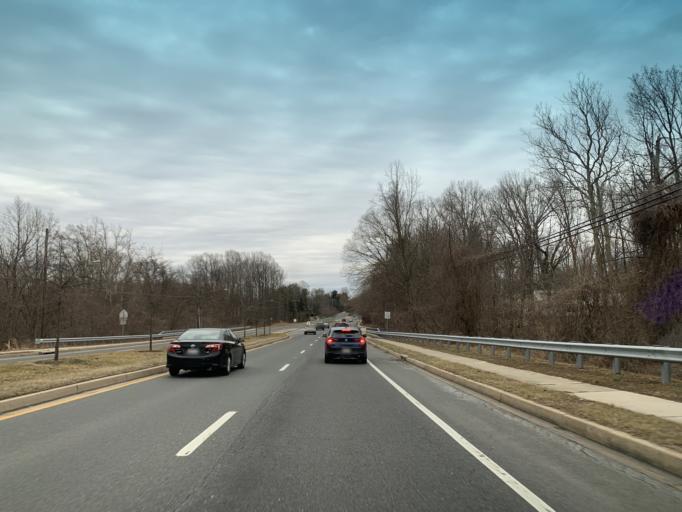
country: US
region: Maryland
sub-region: Montgomery County
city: Layhill
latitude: 39.0762
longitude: -77.0460
